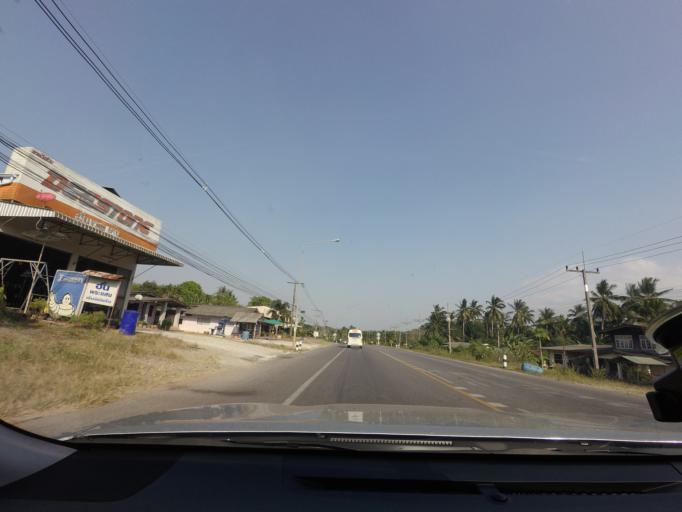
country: TH
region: Surat Thani
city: Phrasaeng
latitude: 8.5735
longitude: 99.2157
